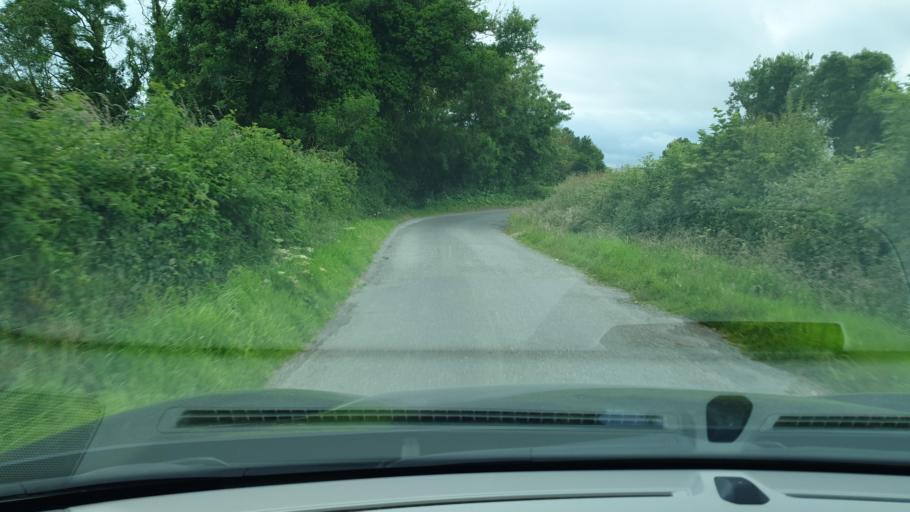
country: IE
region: Leinster
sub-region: An Mhi
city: Dunshaughlin
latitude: 53.5365
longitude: -6.5150
